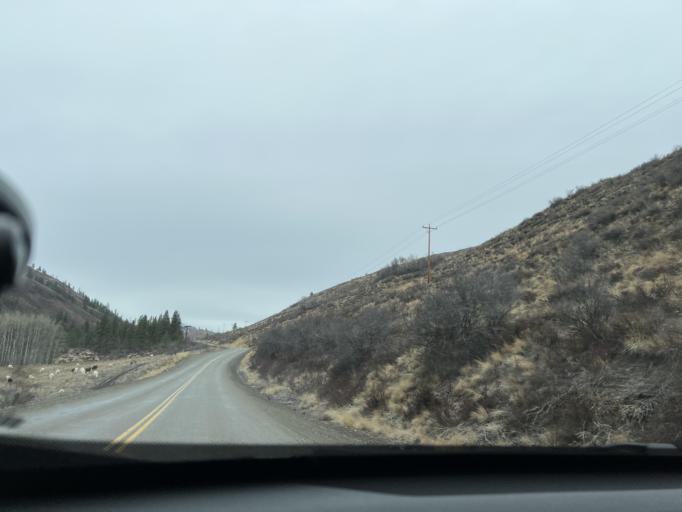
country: US
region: Washington
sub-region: Chelan County
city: Granite Falls
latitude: 48.4485
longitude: -120.2383
